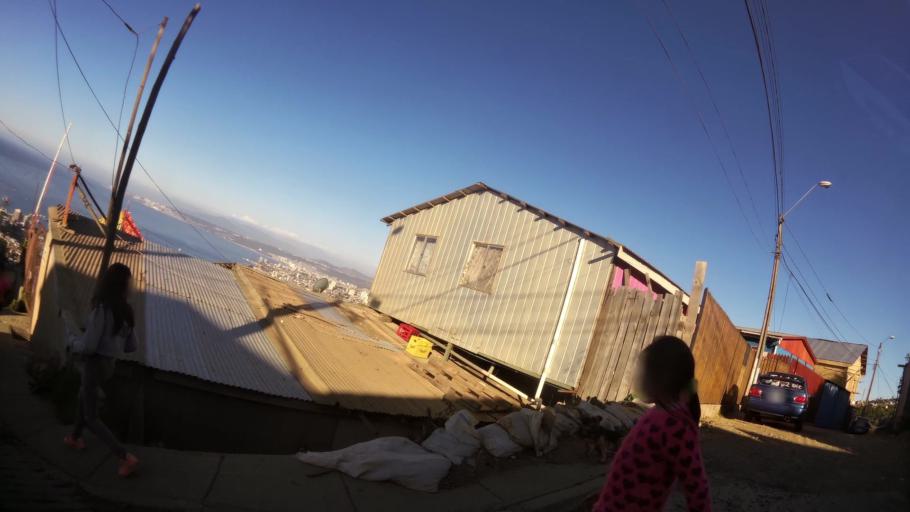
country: CL
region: Valparaiso
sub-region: Provincia de Valparaiso
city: Valparaiso
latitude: -33.0587
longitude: -71.6294
